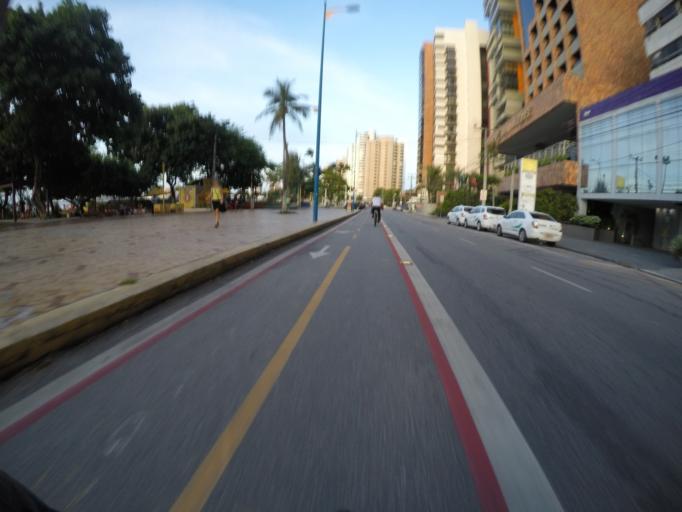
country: BR
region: Ceara
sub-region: Fortaleza
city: Fortaleza
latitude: -3.7232
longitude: -38.4858
